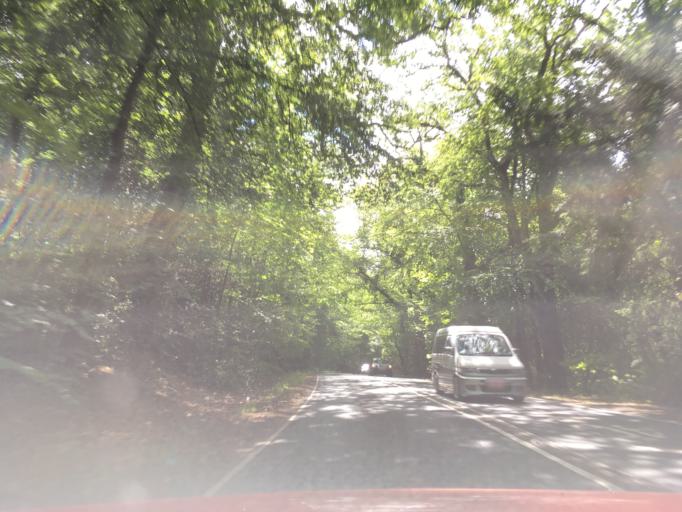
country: GB
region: England
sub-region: Hampshire
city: Highclere
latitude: 51.3511
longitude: -1.3712
